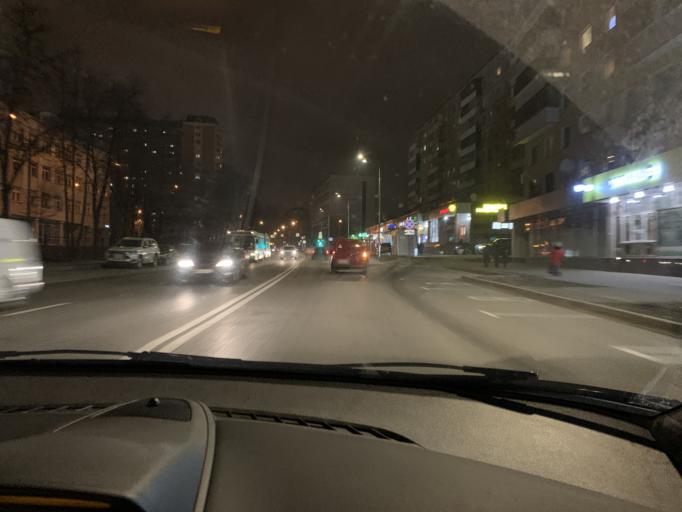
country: RU
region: Moscow
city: Likhobory
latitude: 55.8621
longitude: 37.5675
